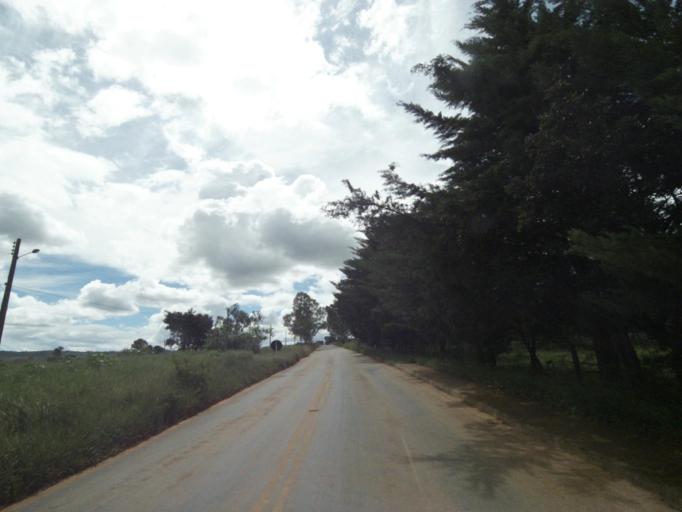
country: BR
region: Goias
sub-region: Pirenopolis
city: Pirenopolis
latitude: -15.7880
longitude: -48.7781
